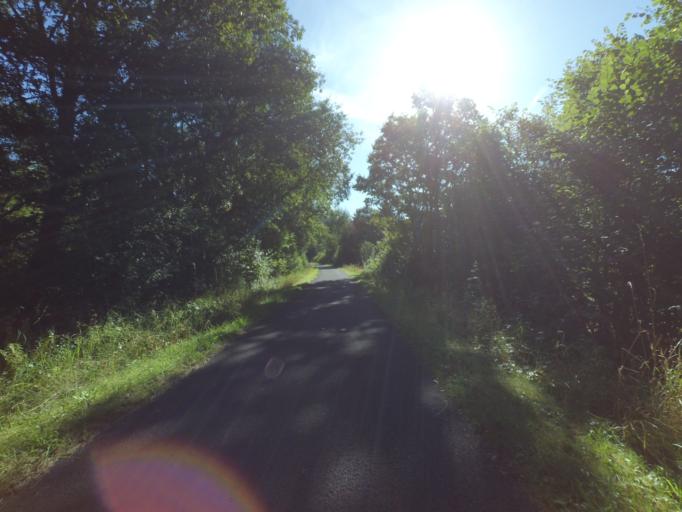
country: DE
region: Rheinland-Pfalz
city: Schalkenmehren
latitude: 50.1841
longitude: 6.8438
